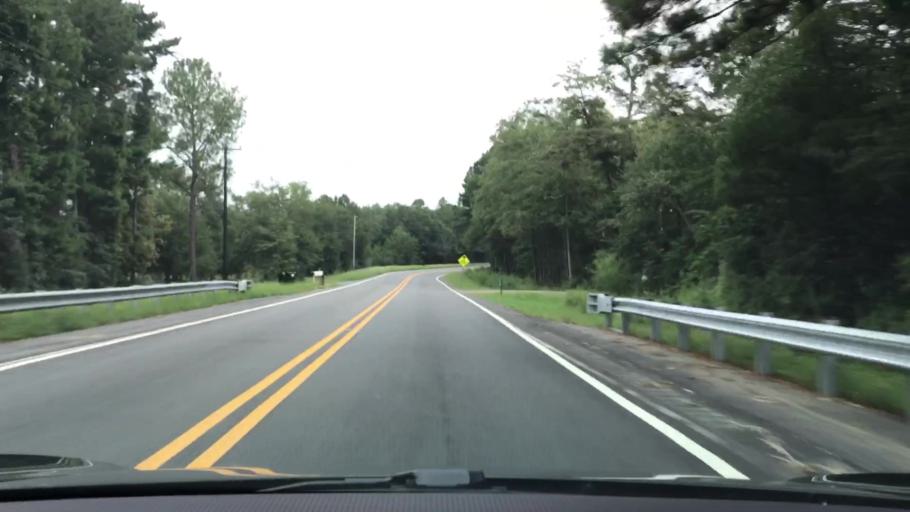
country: US
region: Alabama
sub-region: Covington County
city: Opp
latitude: 31.2261
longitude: -86.1613
